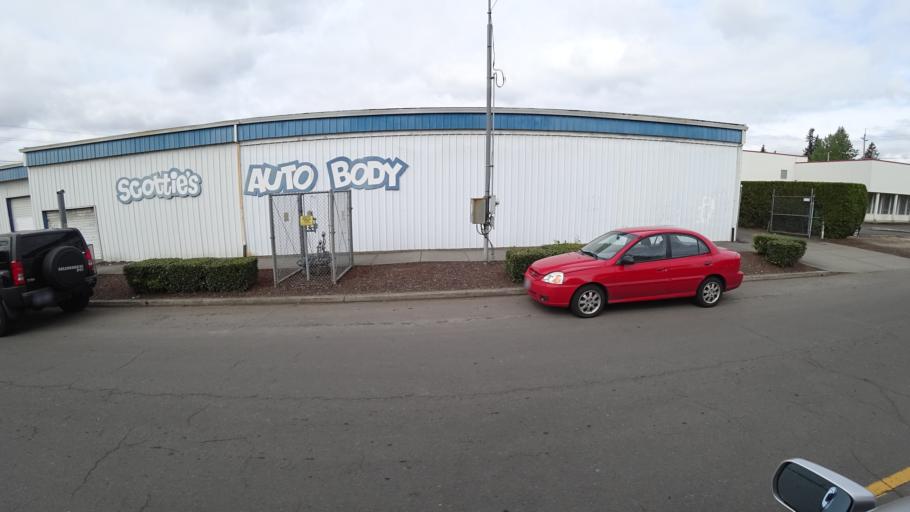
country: US
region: Oregon
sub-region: Washington County
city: Hillsboro
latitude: 45.5206
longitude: -122.9957
